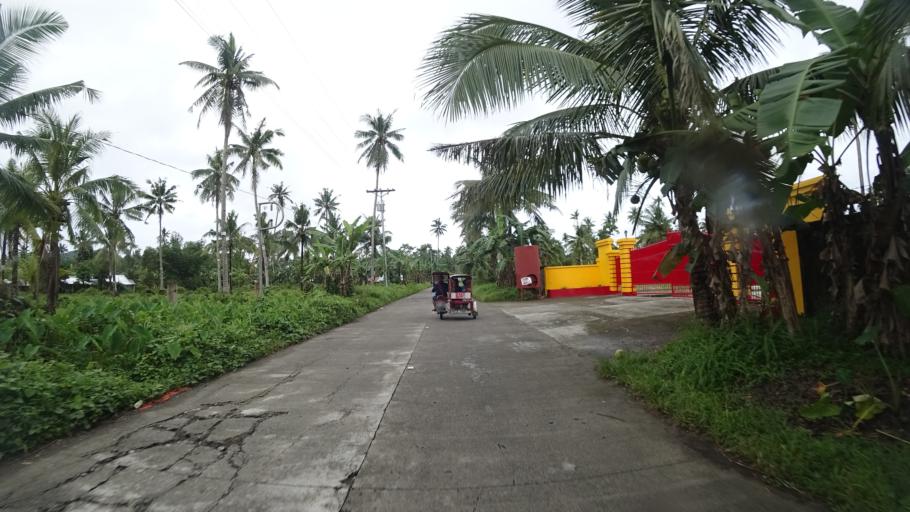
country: PH
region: Eastern Visayas
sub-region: Province of Leyte
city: MacArthur
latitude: 10.8163
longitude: 124.9739
